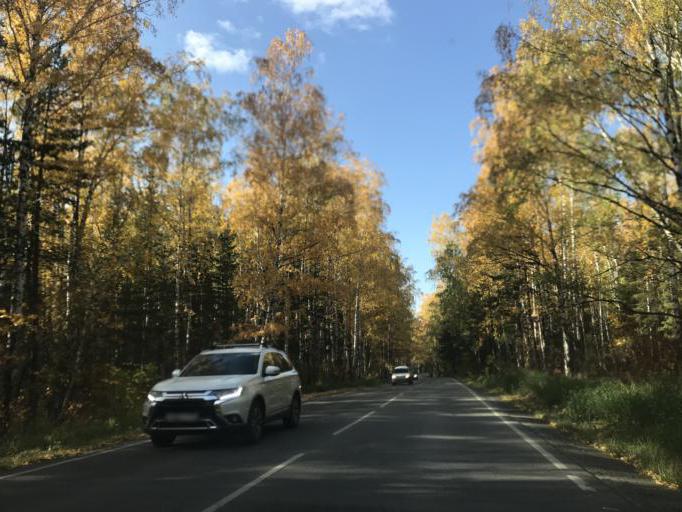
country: RU
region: Chelyabinsk
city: Dolgoderevenskoye
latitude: 55.2828
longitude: 61.3625
